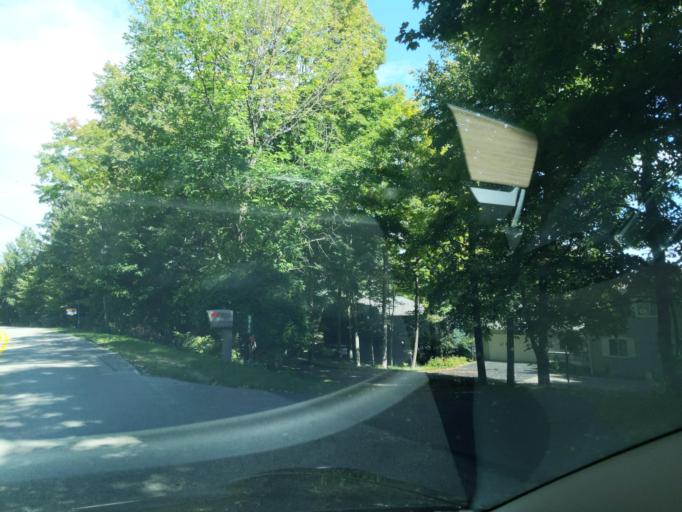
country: US
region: Michigan
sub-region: Antrim County
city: Elk Rapids
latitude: 44.9502
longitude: -85.3225
